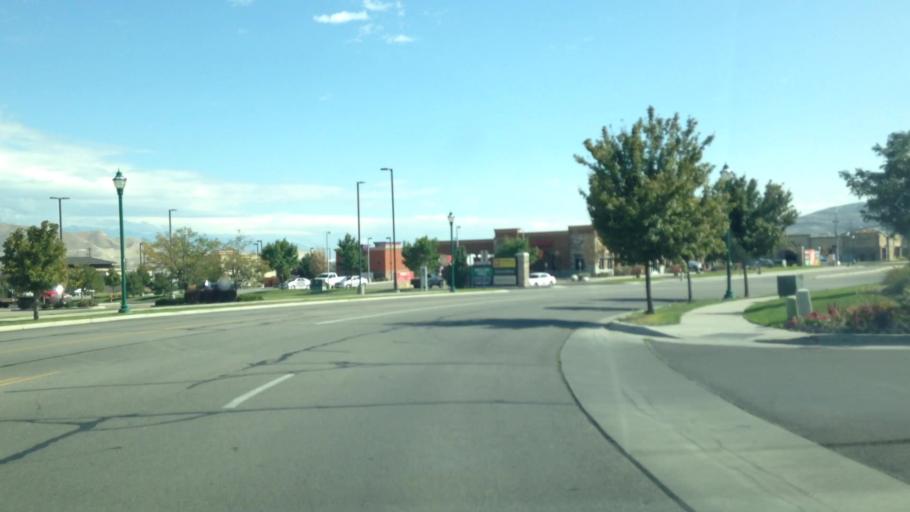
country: US
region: Utah
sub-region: Salt Lake County
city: Riverton
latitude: 40.5094
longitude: -111.9796
